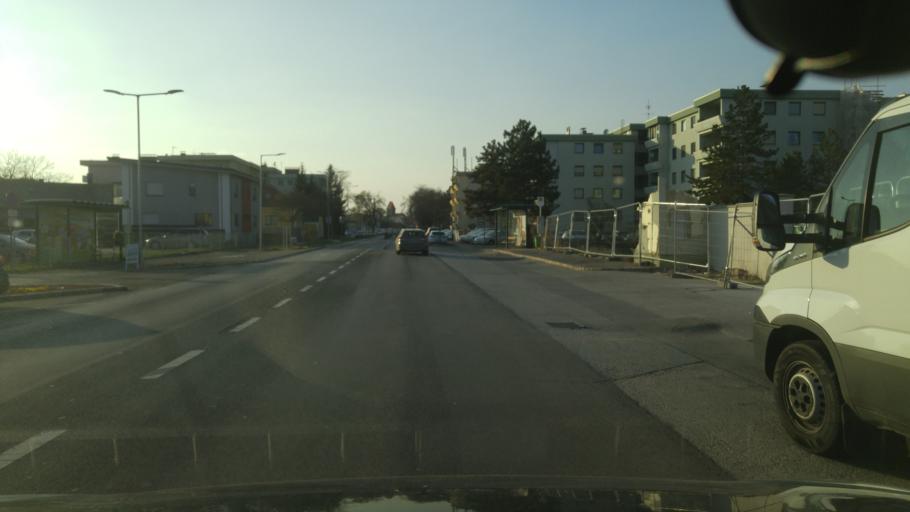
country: AT
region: Lower Austria
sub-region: Politischer Bezirk Wien-Umgebung
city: Himberg
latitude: 48.0770
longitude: 16.4451
